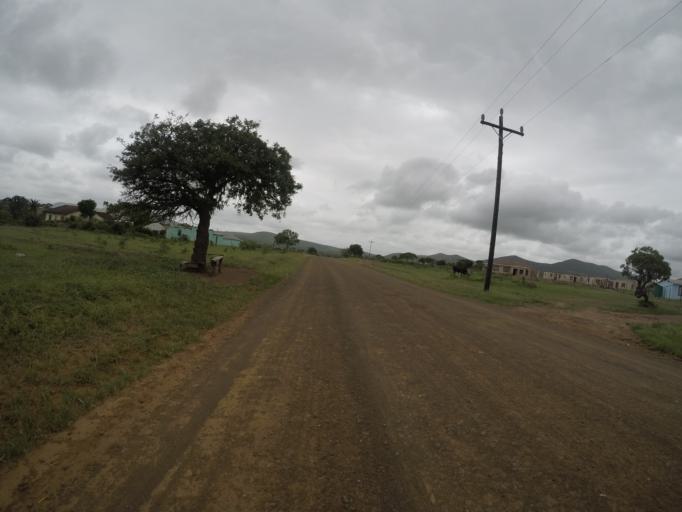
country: ZA
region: KwaZulu-Natal
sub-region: uThungulu District Municipality
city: Empangeni
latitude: -28.6088
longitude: 31.8550
